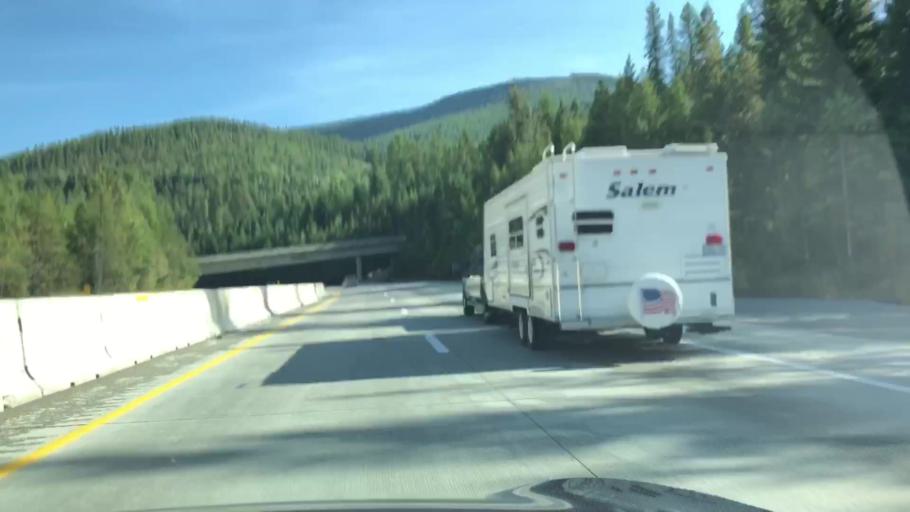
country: US
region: Idaho
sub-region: Shoshone County
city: Wallace
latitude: 47.4677
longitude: -115.7598
